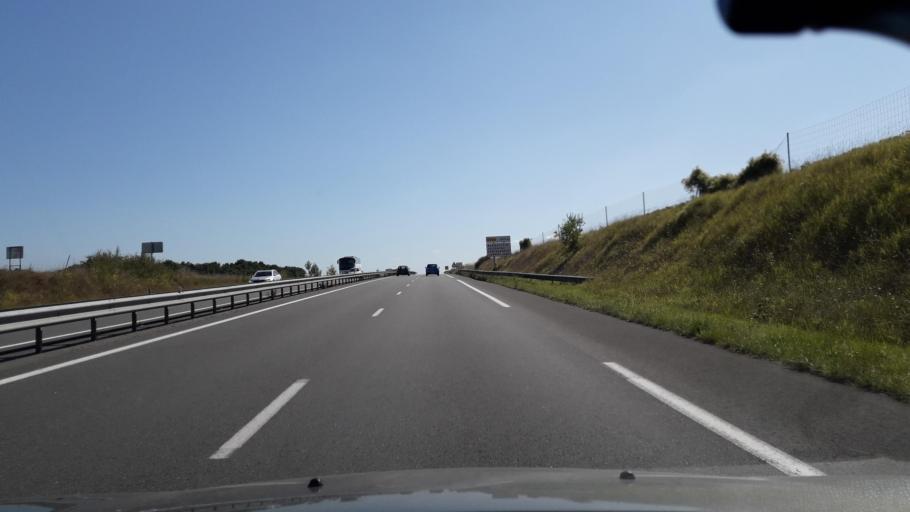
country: FR
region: Poitou-Charentes
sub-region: Departement de la Charente
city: Chassors
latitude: 45.6687
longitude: -0.2055
